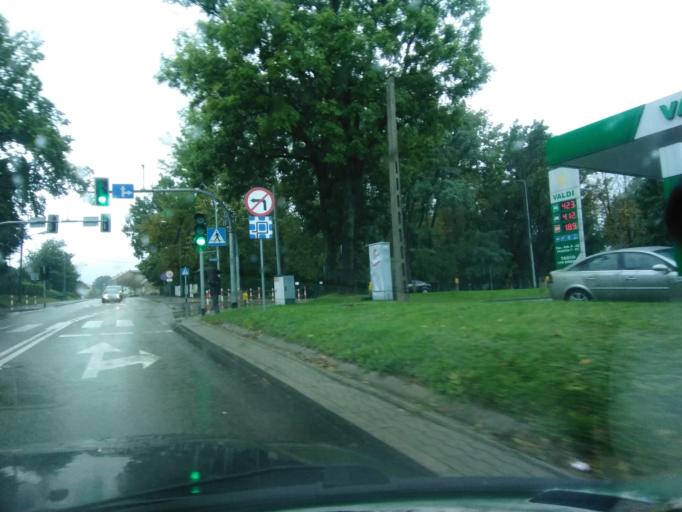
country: PL
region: Subcarpathian Voivodeship
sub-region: Powiat debicki
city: Debica
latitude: 50.0548
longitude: 21.4100
